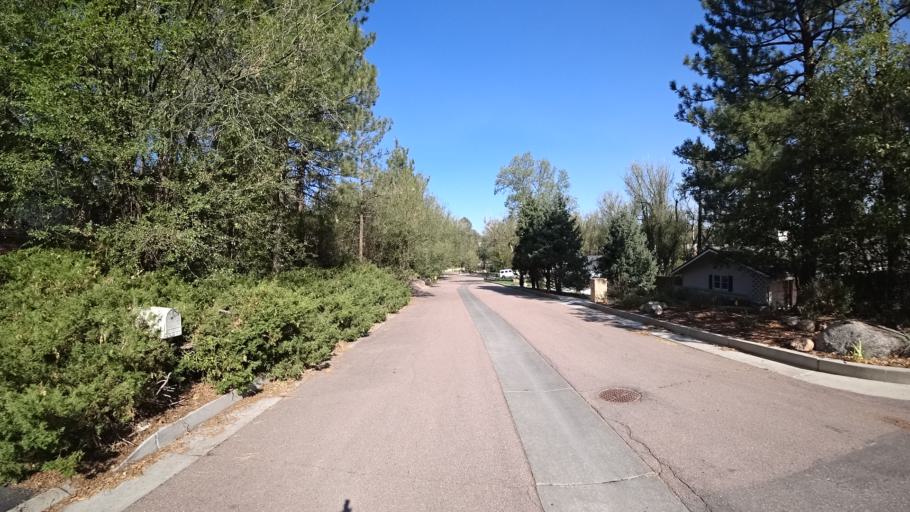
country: US
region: Colorado
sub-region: El Paso County
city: Colorado Springs
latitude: 38.7976
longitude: -104.8490
